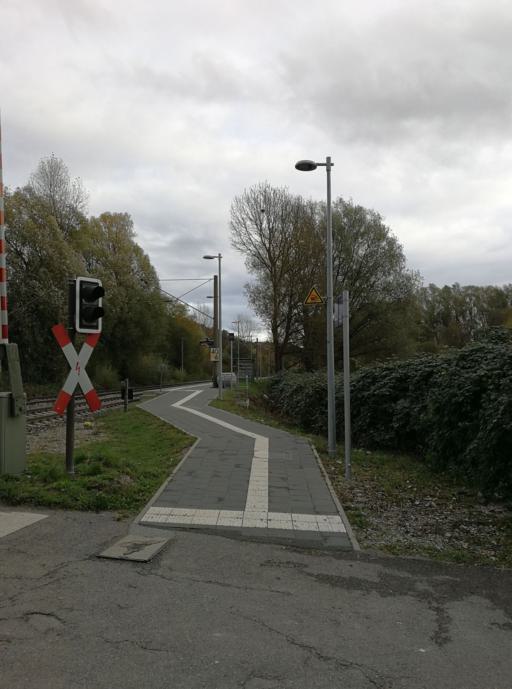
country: DE
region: Baden-Wuerttemberg
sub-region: Freiburg Region
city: Allensbach
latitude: 47.7059
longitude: 9.0995
